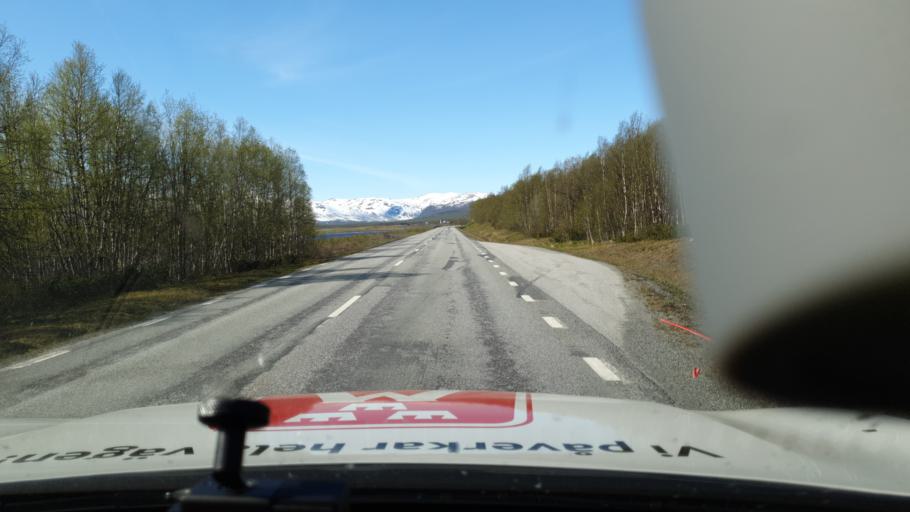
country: NO
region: Nordland
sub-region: Rana
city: Mo i Rana
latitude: 65.7930
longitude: 15.1020
